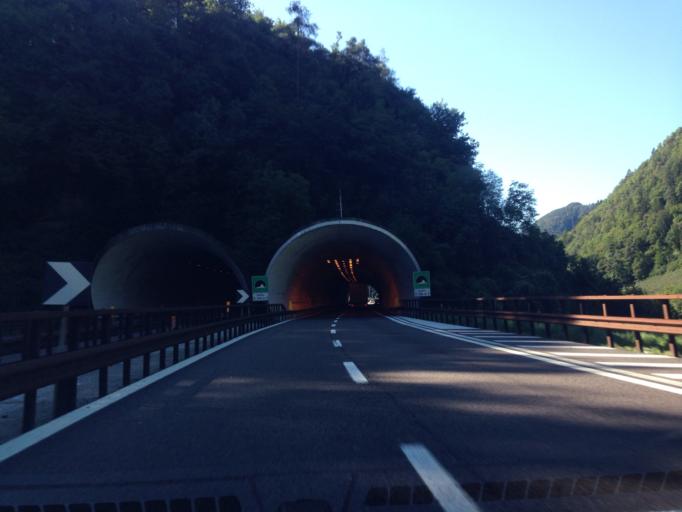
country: IT
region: Trentino-Alto Adige
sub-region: Bolzano
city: Ponte Gardena
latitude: 46.5743
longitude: 11.5235
